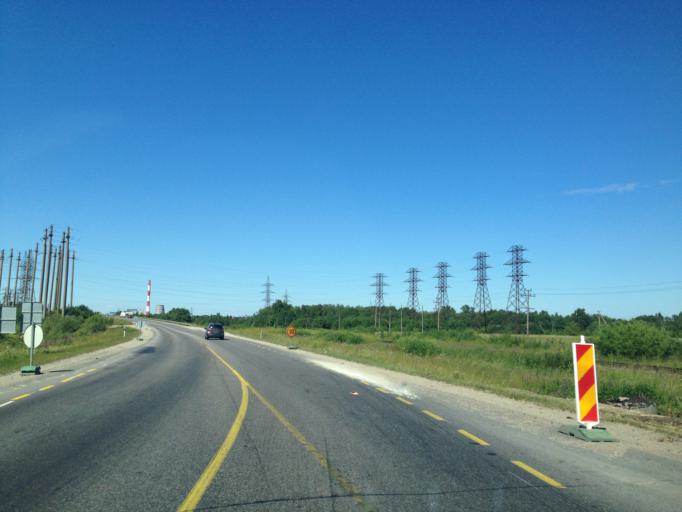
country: EE
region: Harju
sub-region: Joelaehtme vald
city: Loo
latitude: 59.4203
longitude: 24.9208
